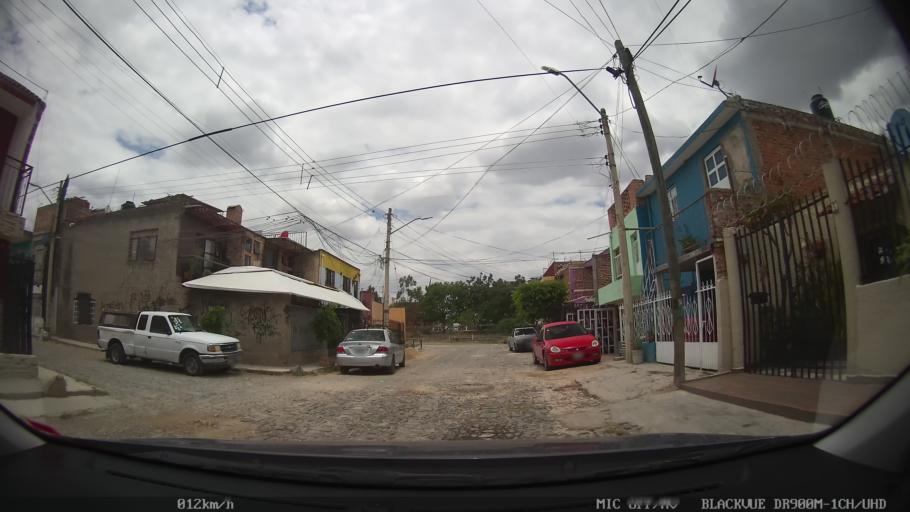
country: MX
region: Jalisco
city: Tlaquepaque
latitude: 20.6537
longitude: -103.2673
